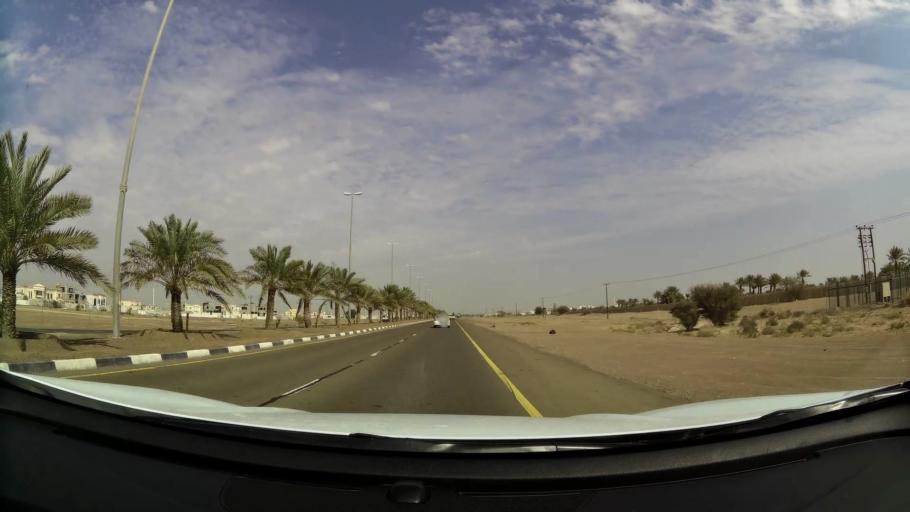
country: AE
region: Abu Dhabi
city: Al Ain
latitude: 24.0902
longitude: 55.8539
